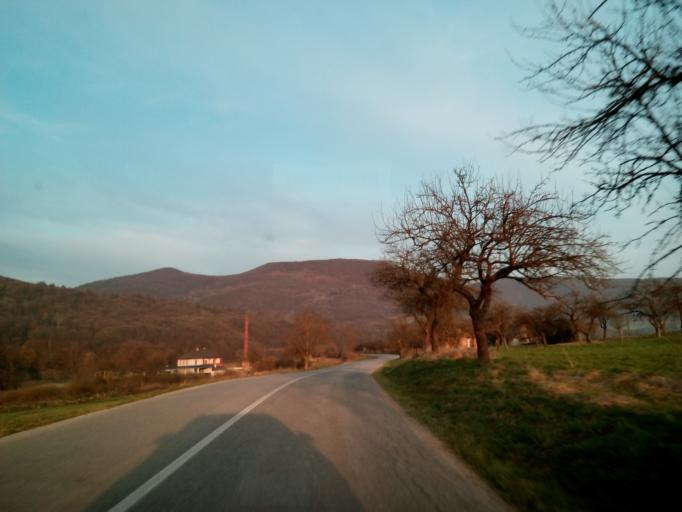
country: SK
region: Kosicky
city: Dobsina
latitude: 48.6774
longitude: 20.3499
